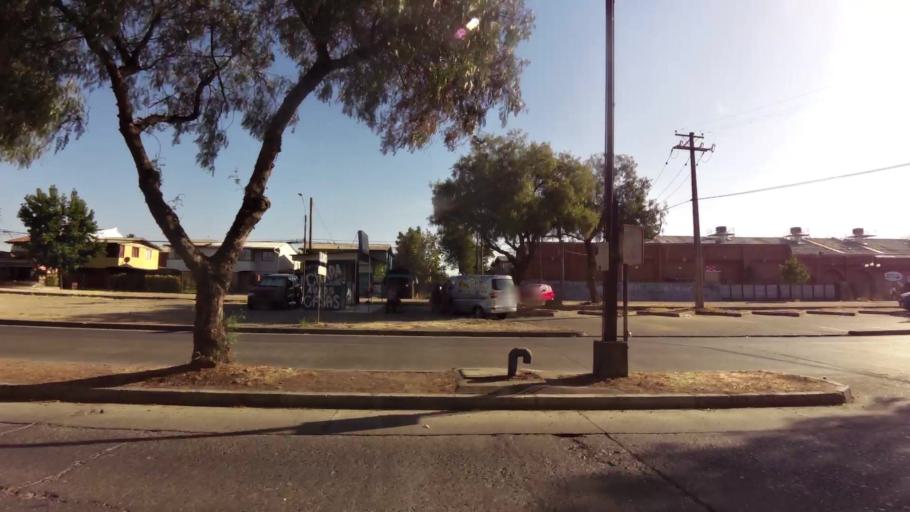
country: CL
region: Maule
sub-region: Provincia de Talca
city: Talca
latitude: -35.4390
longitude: -71.6808
